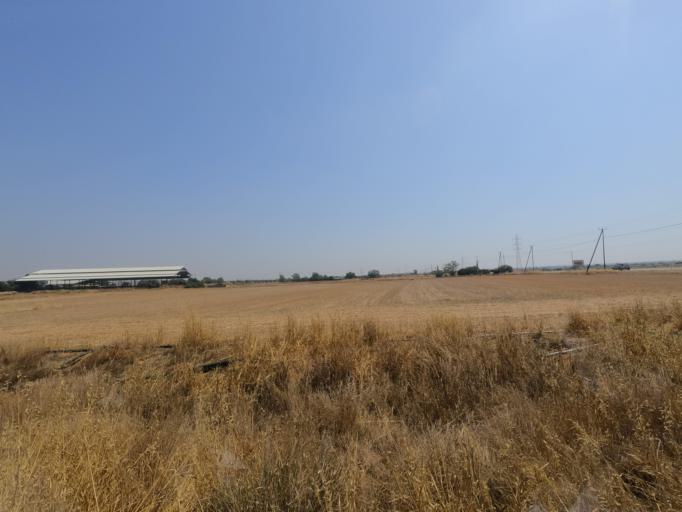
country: CY
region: Ammochostos
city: Avgorou
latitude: 35.0167
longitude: 33.8226
